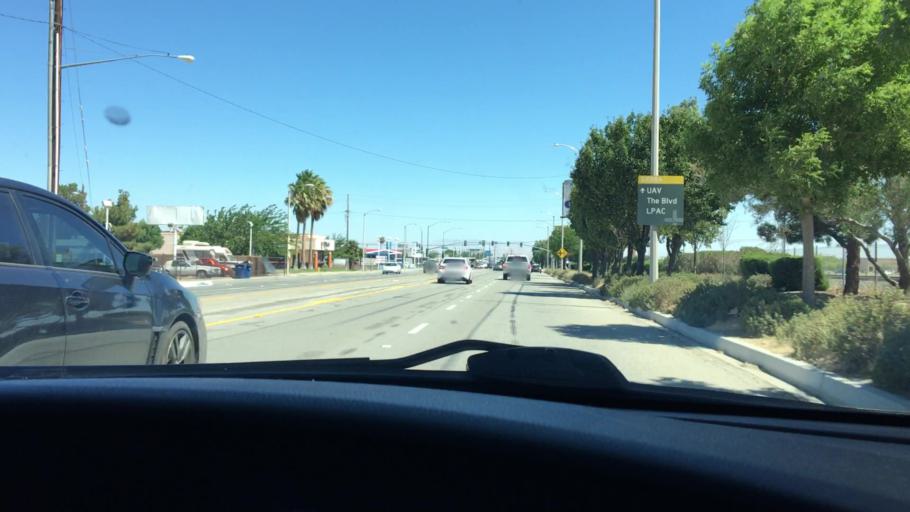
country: US
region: California
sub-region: Los Angeles County
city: Lancaster
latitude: 34.6730
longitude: -118.1325
